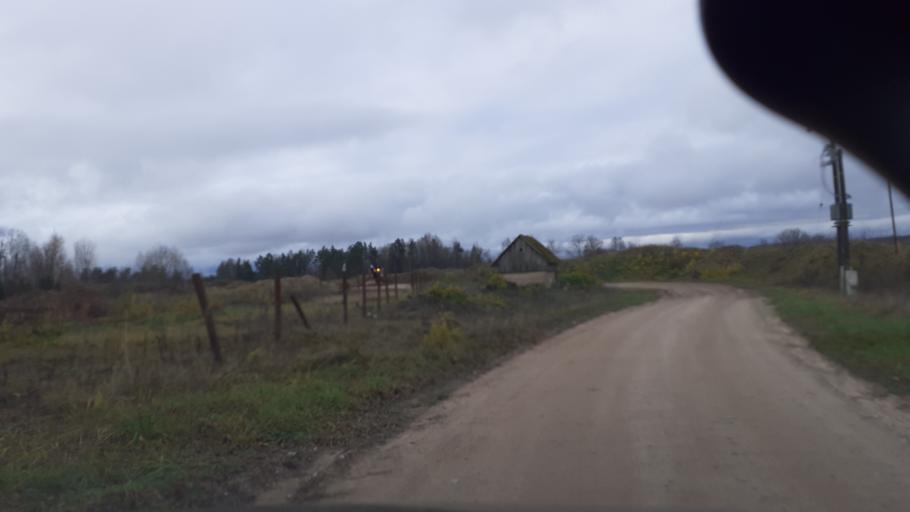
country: LV
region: Kuldigas Rajons
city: Kuldiga
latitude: 57.0456
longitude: 21.8690
